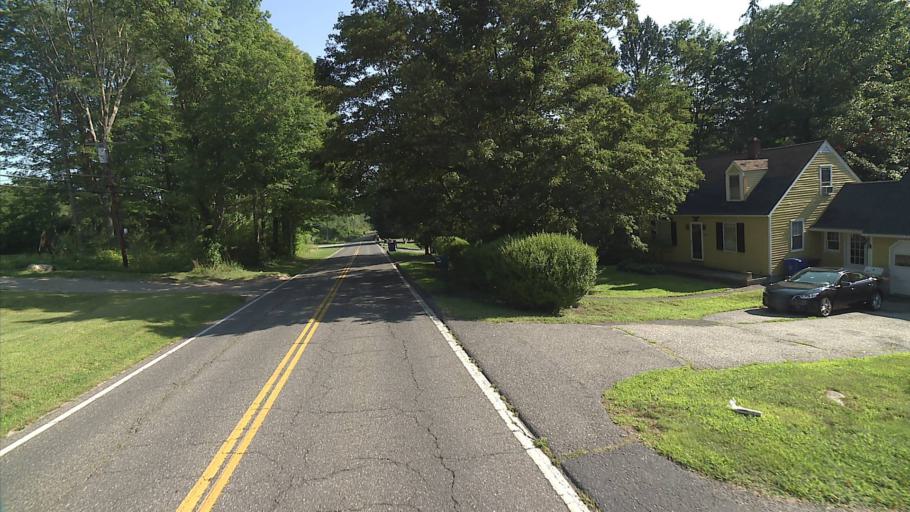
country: US
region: Connecticut
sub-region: Litchfield County
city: Winsted
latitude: 41.8688
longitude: -73.0687
